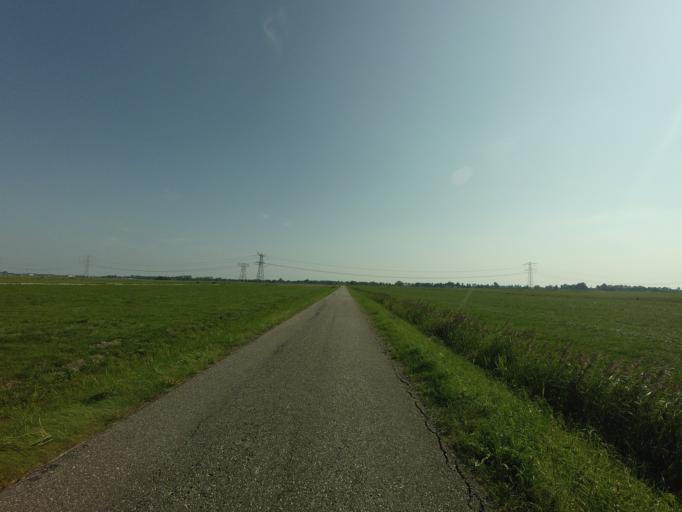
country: NL
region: Groningen
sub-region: Gemeente Zuidhorn
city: Zuidhorn
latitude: 53.2199
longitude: 6.4292
